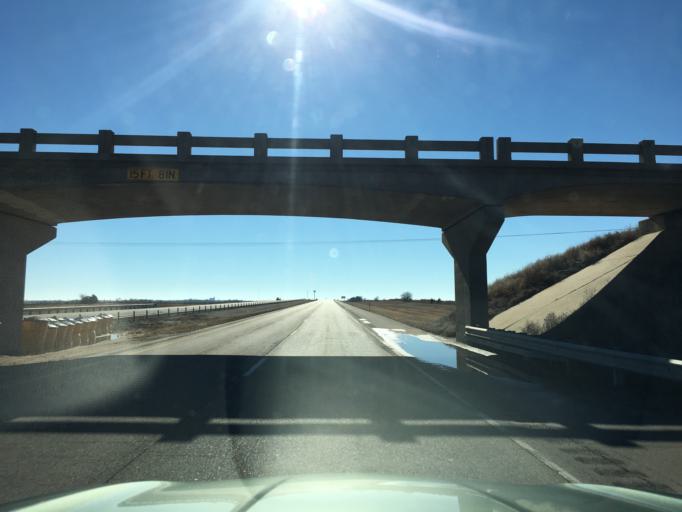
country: US
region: Oklahoma
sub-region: Kay County
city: Blackwell
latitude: 36.9708
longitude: -97.3458
